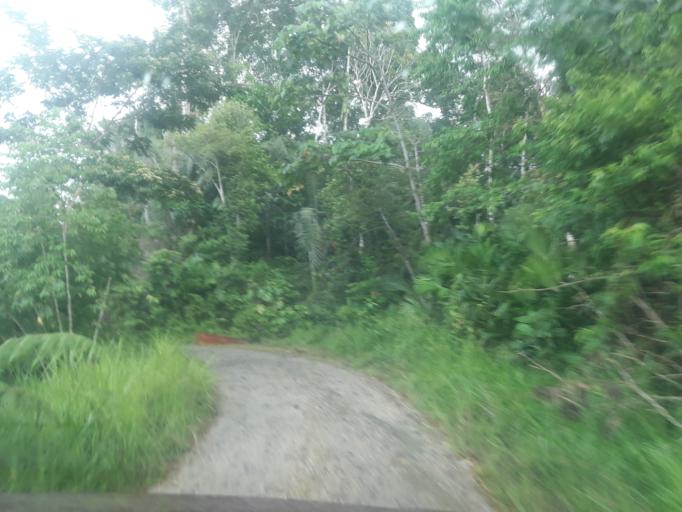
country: EC
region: Napo
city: Tena
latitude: -1.0950
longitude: -77.6996
